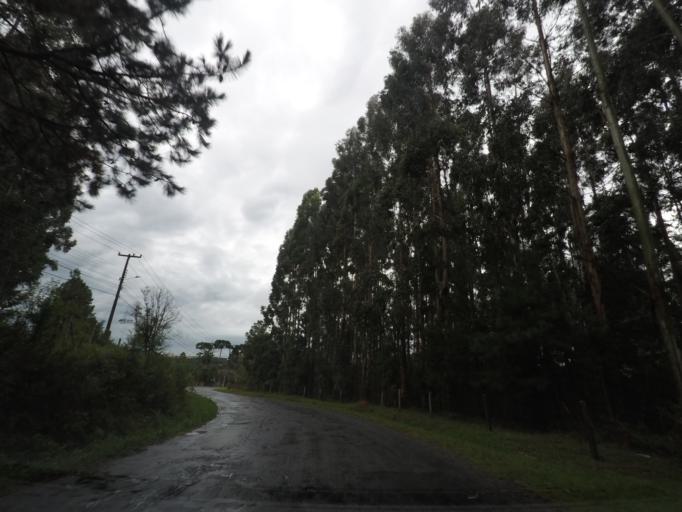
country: BR
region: Parana
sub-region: Campo Largo
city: Campo Largo
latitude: -25.4516
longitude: -49.4390
